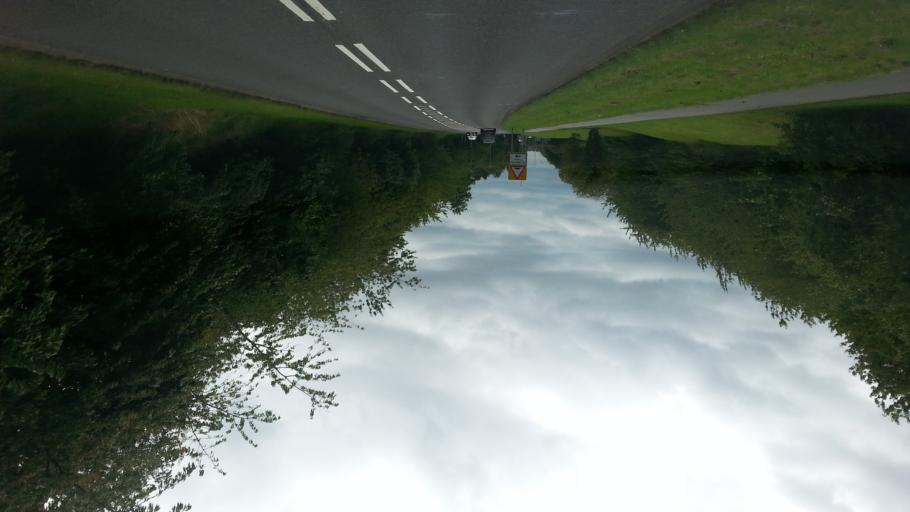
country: GB
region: England
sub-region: Northamptonshire
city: Earls Barton
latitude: 52.2676
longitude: -0.8122
